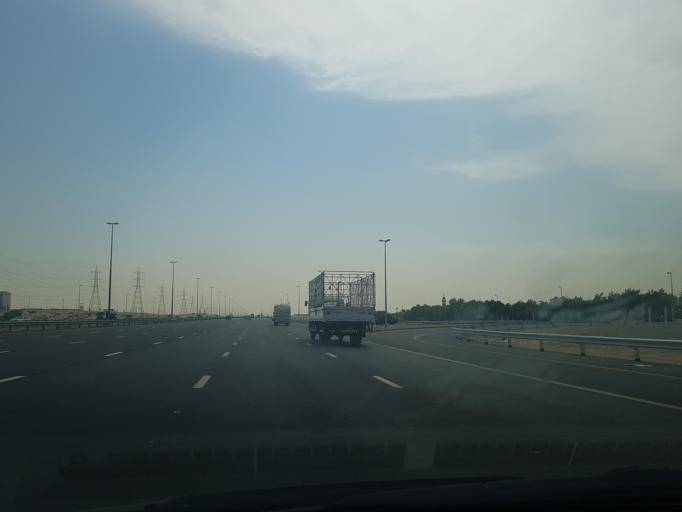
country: AE
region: Ash Shariqah
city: Sharjah
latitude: 25.2684
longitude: 55.5802
